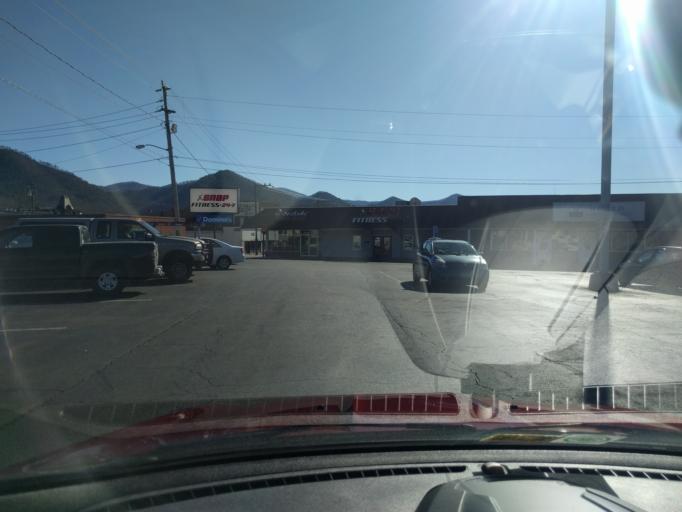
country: US
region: Virginia
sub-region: City of Buena Vista
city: Buena Vista
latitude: 37.7363
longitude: -79.3551
